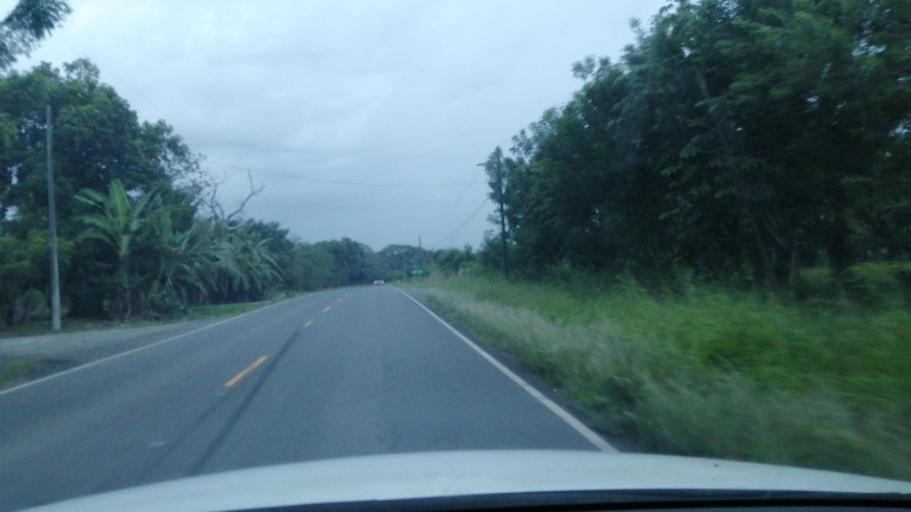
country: PA
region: Chiriqui
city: Alanje
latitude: 8.3966
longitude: -82.4885
